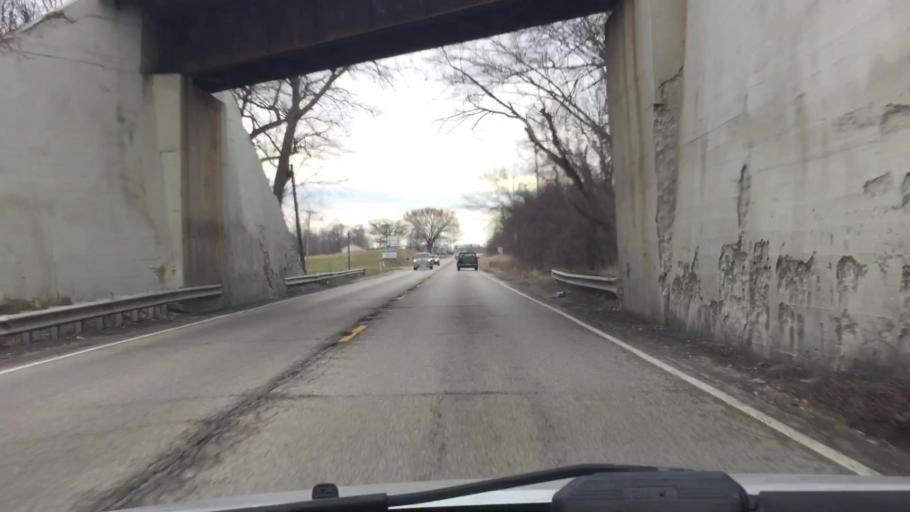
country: US
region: Illinois
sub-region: McHenry County
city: Richmond
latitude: 42.4564
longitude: -88.3059
